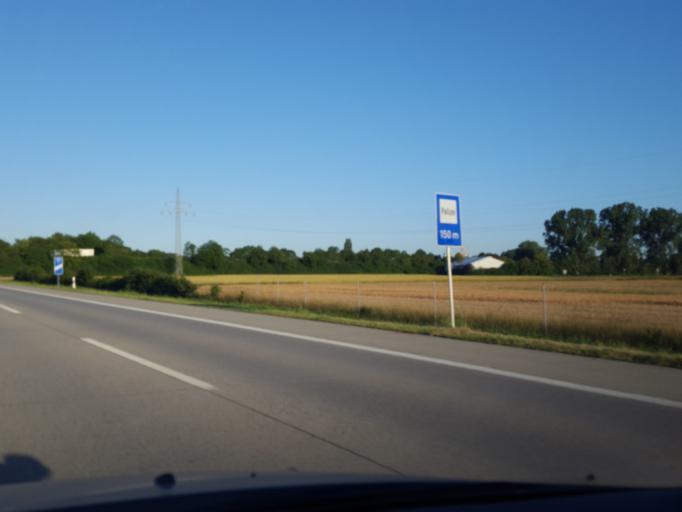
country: DE
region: Bavaria
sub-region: Upper Bavaria
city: Marzling
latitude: 48.3885
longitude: 11.7824
